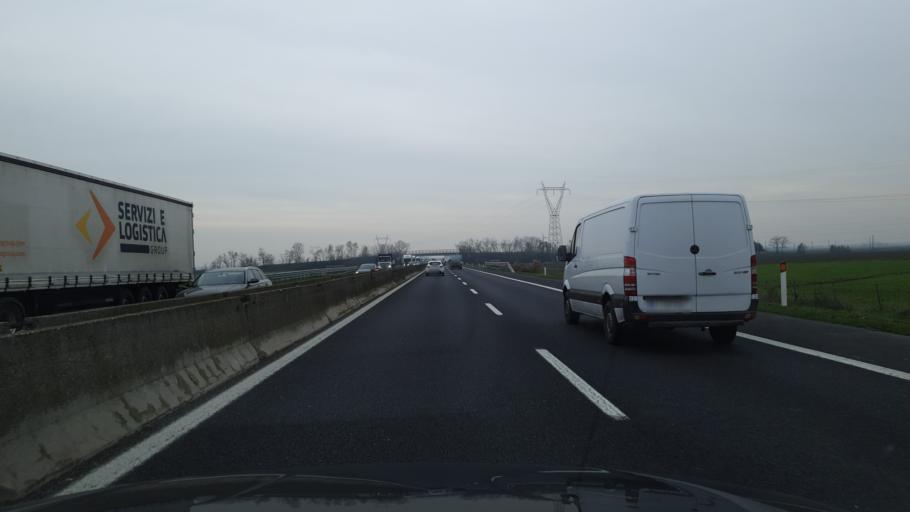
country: IT
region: Emilia-Romagna
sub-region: Provincia di Ferrara
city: San Martino
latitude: 44.7769
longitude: 11.5466
